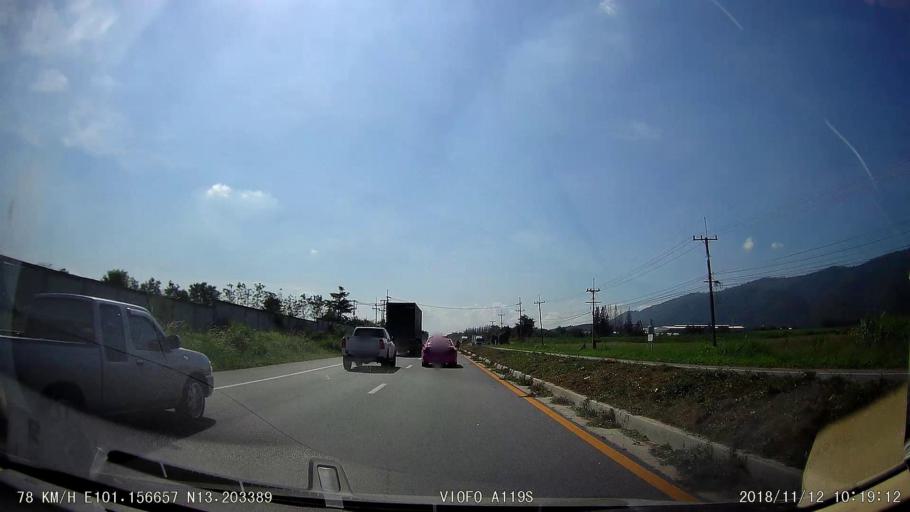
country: TH
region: Chon Buri
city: Ban Bueng
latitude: 13.2030
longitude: 101.1567
